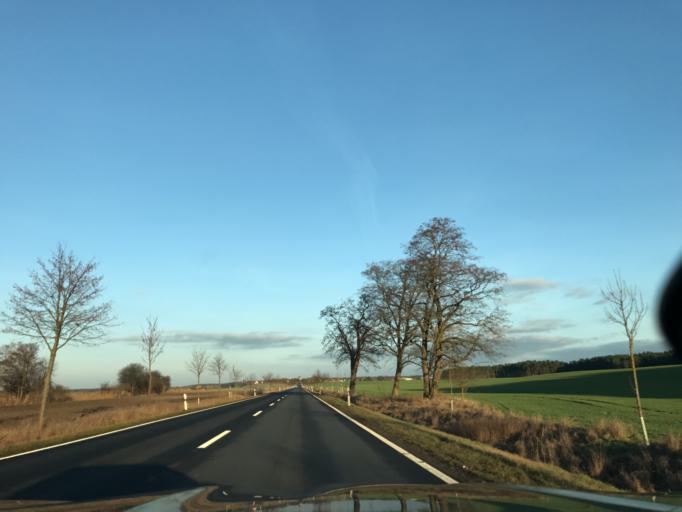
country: DE
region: Saxony-Anhalt
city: Burg bei Magdeburg
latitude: 52.3015
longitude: 11.9842
